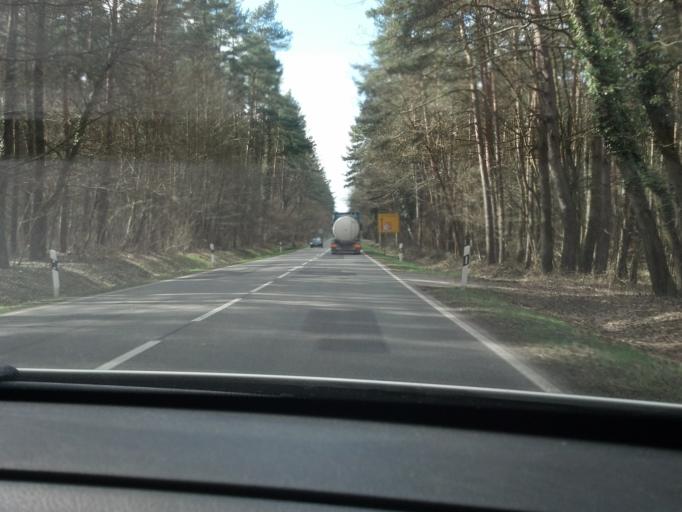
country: DE
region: Mecklenburg-Vorpommern
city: Plau am See
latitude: 53.3799
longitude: 12.3318
